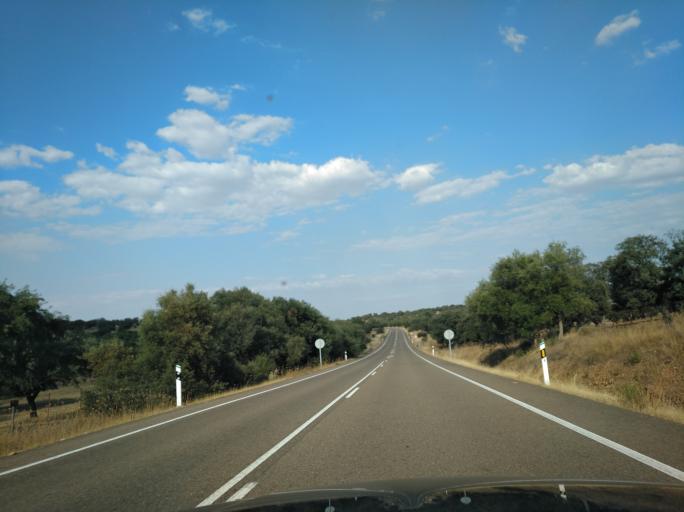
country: ES
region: Extremadura
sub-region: Provincia de Badajoz
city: Alconchel
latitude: 38.4449
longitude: -7.0950
